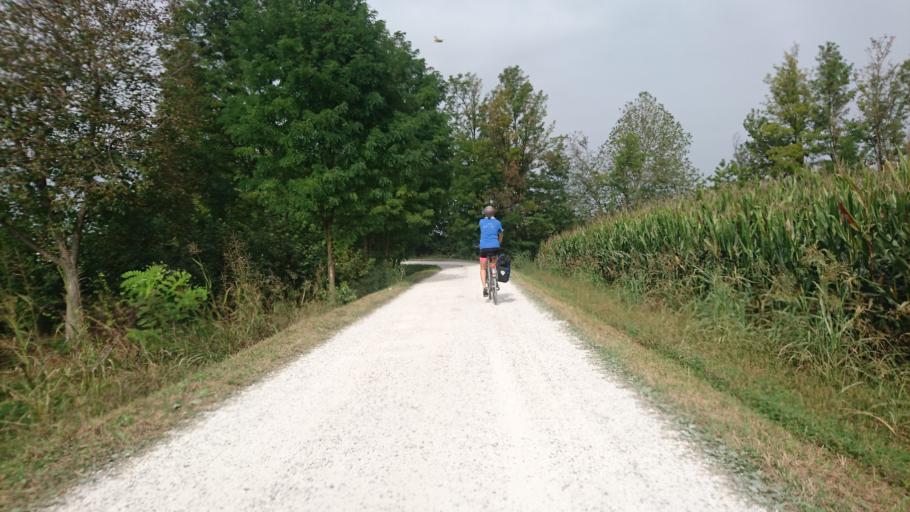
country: IT
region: Veneto
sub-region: Provincia di Padova
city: Grantorto
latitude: 45.5811
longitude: 11.7544
